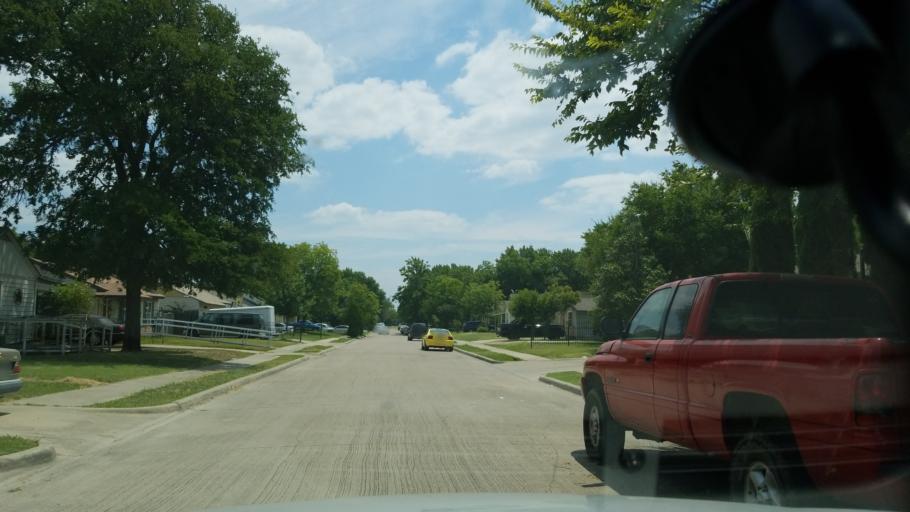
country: US
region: Texas
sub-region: Dallas County
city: Grand Prairie
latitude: 32.7496
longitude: -96.9839
